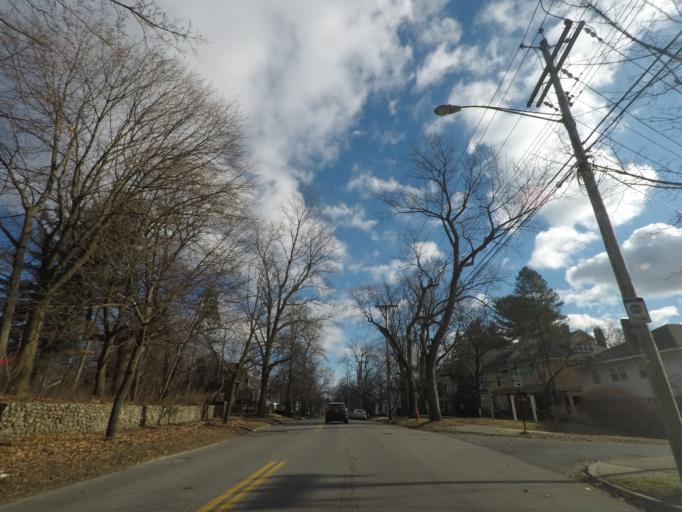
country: US
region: New York
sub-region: Schenectady County
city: Schenectady
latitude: 42.8097
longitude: -73.9180
